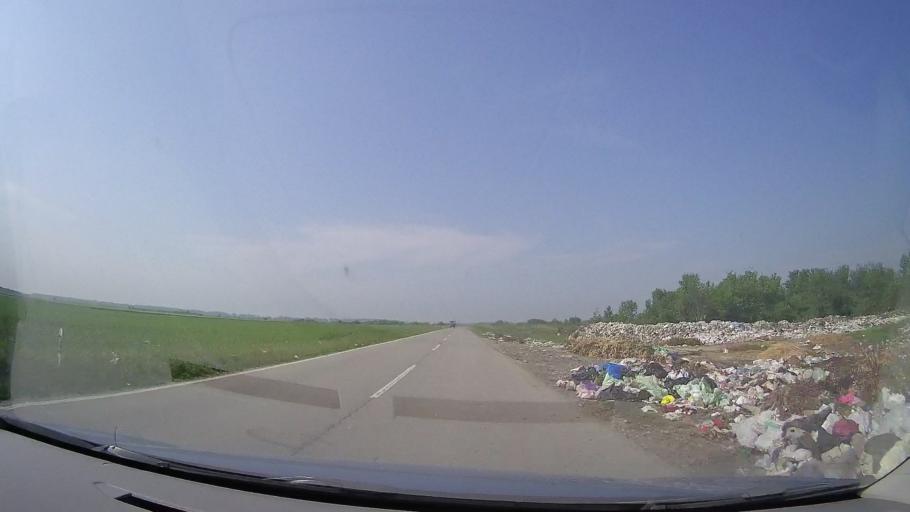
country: RS
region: Autonomna Pokrajina Vojvodina
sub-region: Srednjebanatski Okrug
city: Secanj
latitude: 45.3912
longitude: 20.8033
